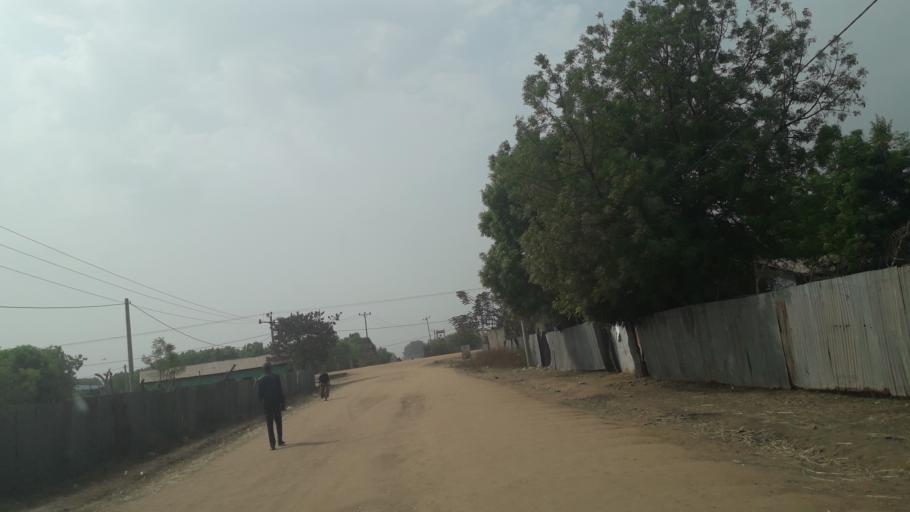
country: ET
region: Gambela
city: Gambela
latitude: 8.2991
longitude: 33.6828
